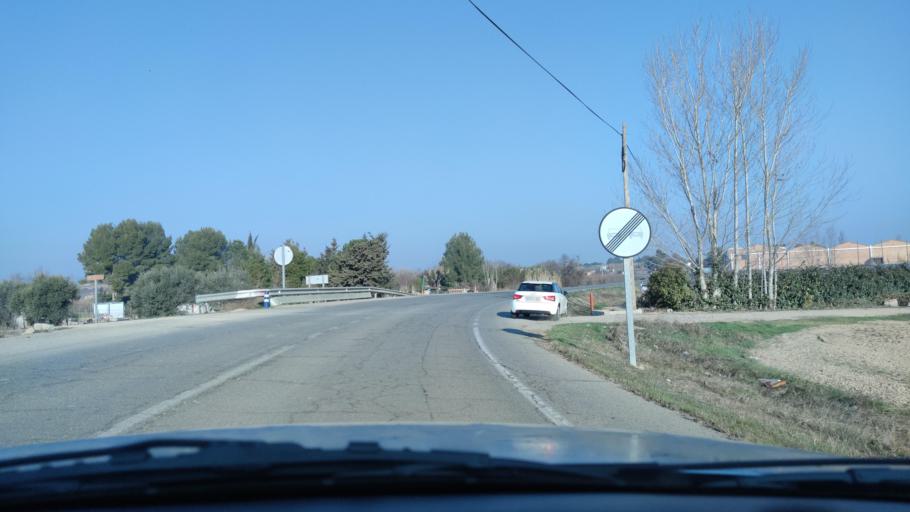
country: ES
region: Catalonia
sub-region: Provincia de Lleida
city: Torrefarrera
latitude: 41.6577
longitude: 0.6312
